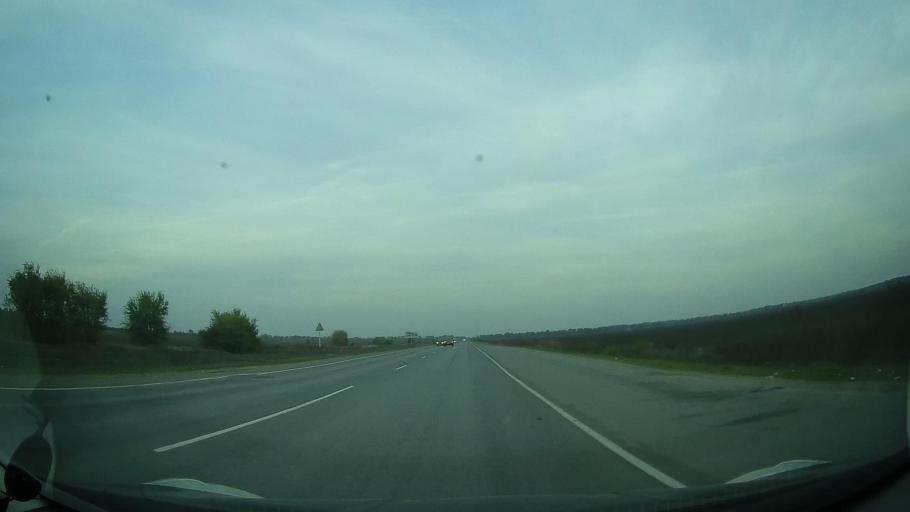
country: RU
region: Rostov
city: Ol'ginskaya
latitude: 47.1299
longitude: 39.9058
